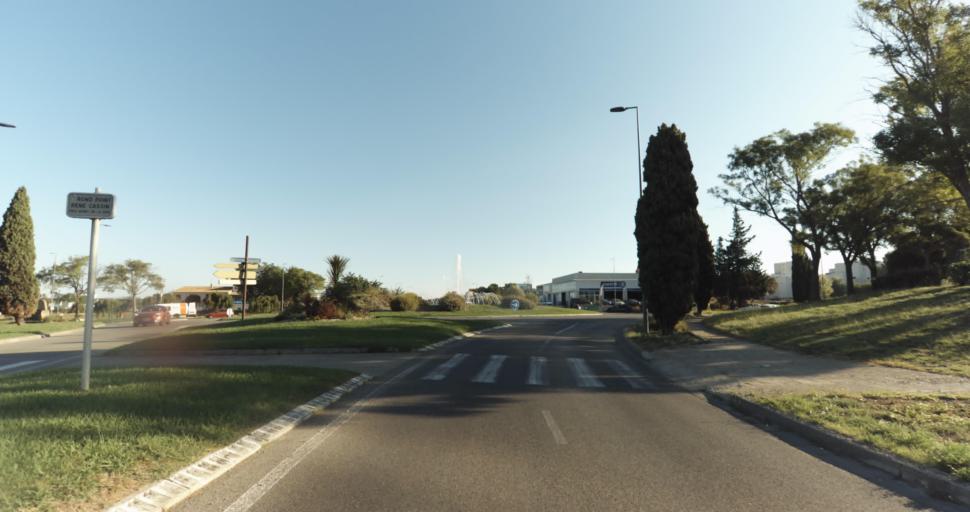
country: FR
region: Provence-Alpes-Cote d'Azur
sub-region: Departement des Bouches-du-Rhone
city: Miramas
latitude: 43.5981
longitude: 5.0058
